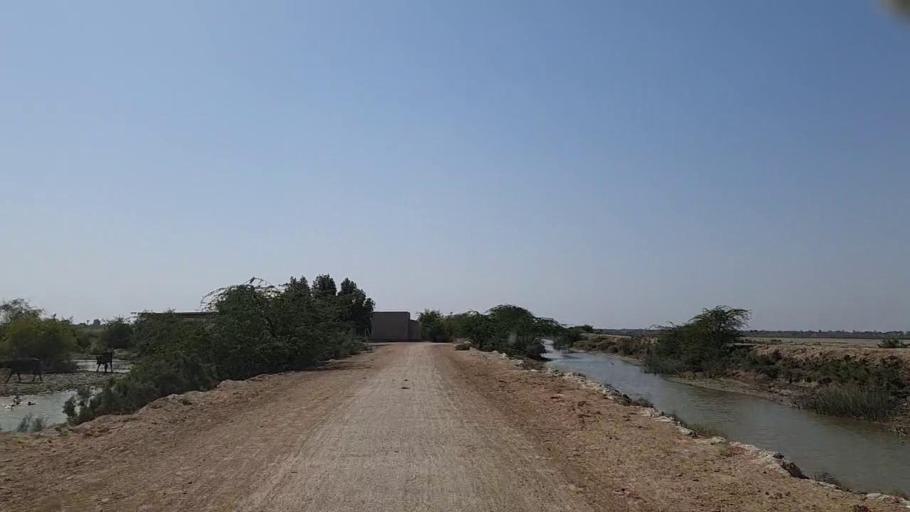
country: PK
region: Sindh
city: Mirpur Batoro
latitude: 24.6719
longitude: 68.3058
